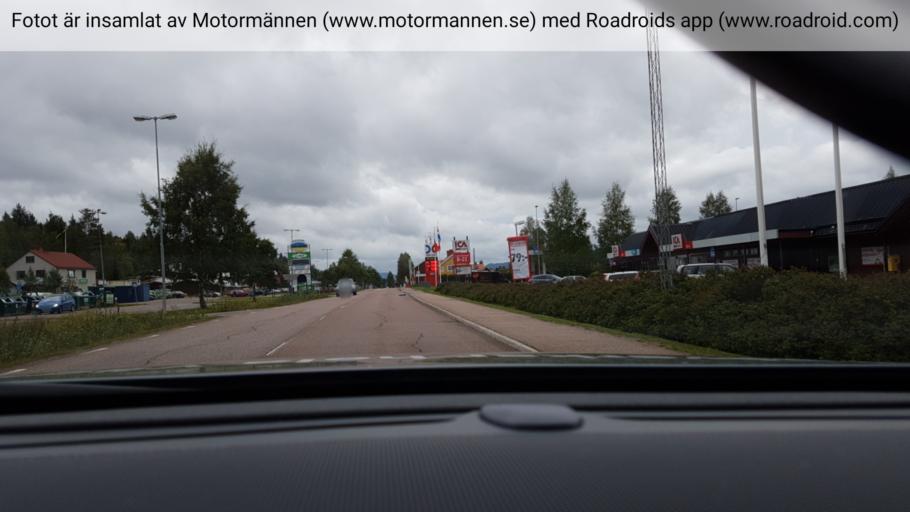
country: SE
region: Dalarna
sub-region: Malung-Saelens kommun
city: Malung
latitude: 61.1578
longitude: 13.2658
